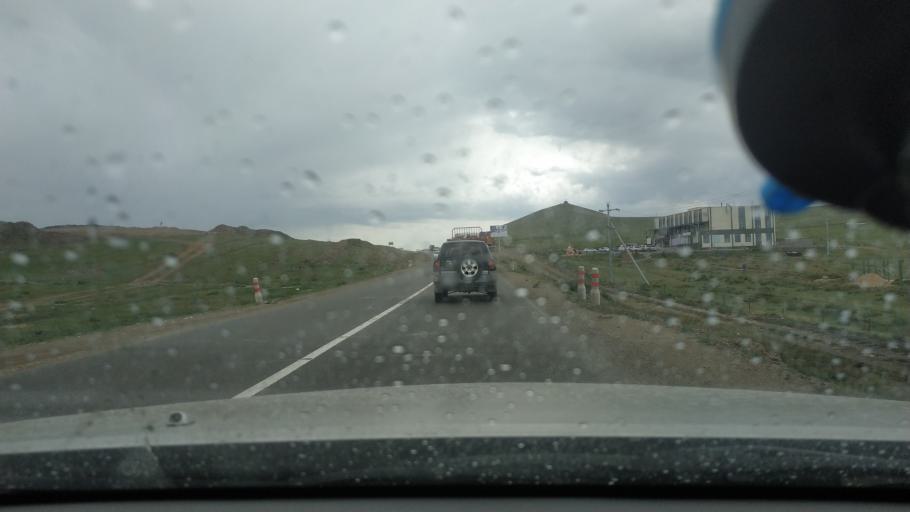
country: MN
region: Ulaanbaatar
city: Ulaanbaatar
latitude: 47.7912
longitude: 106.7460
